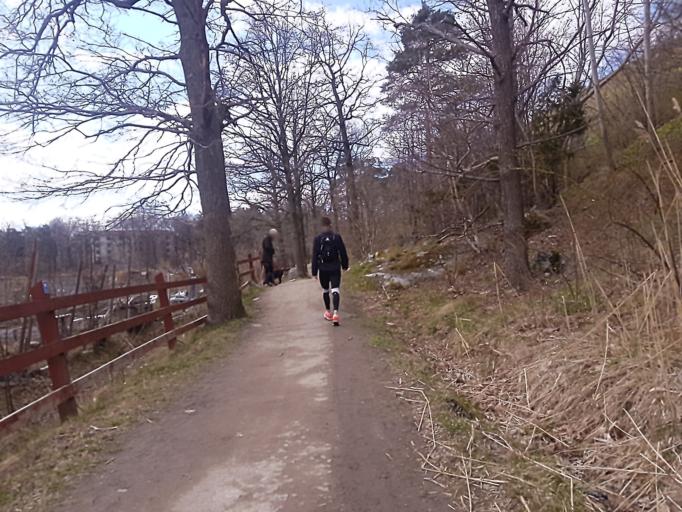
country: SE
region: Stockholm
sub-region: Stockholms Kommun
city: OEstermalm
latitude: 59.2991
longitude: 18.1125
